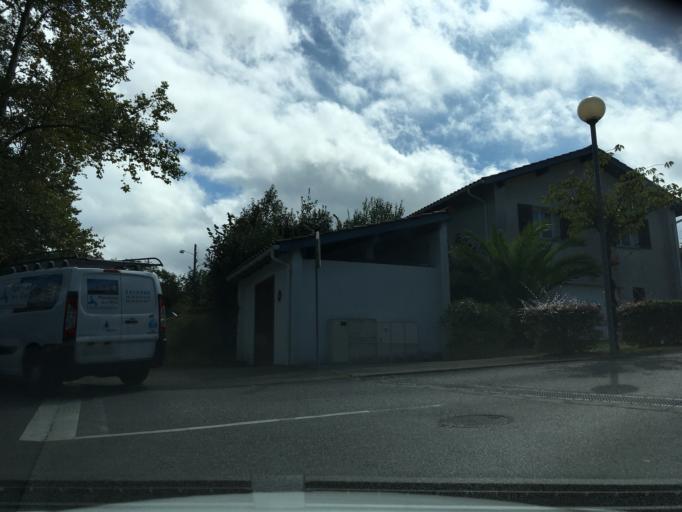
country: FR
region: Aquitaine
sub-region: Departement des Pyrenees-Atlantiques
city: Boucau
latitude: 43.4991
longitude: -1.4498
